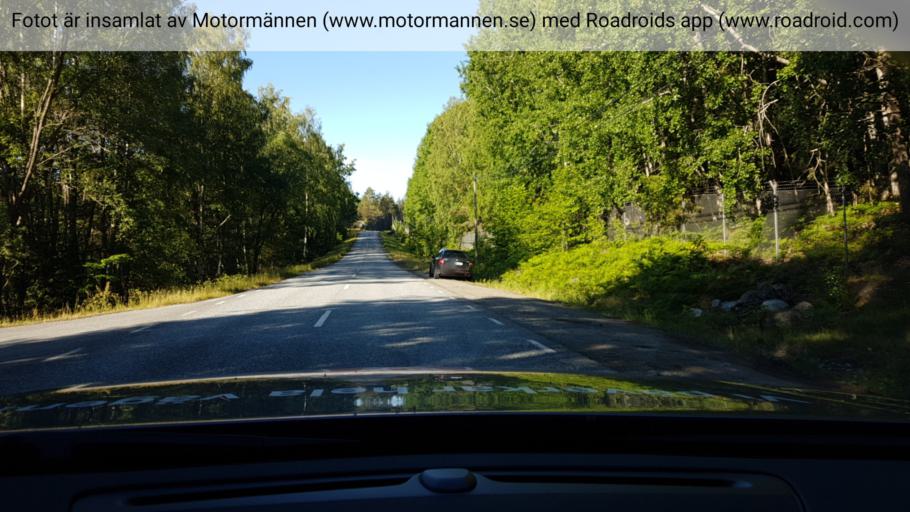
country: SE
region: Stockholm
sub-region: Nynashamns Kommun
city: Nynashamn
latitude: 58.9781
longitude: 18.0814
